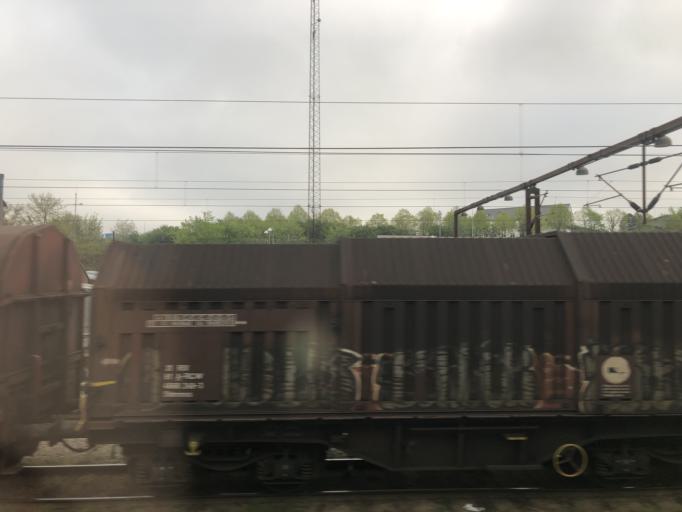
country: DK
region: South Denmark
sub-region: Fredericia Kommune
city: Fredericia
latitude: 55.5774
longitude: 9.7380
